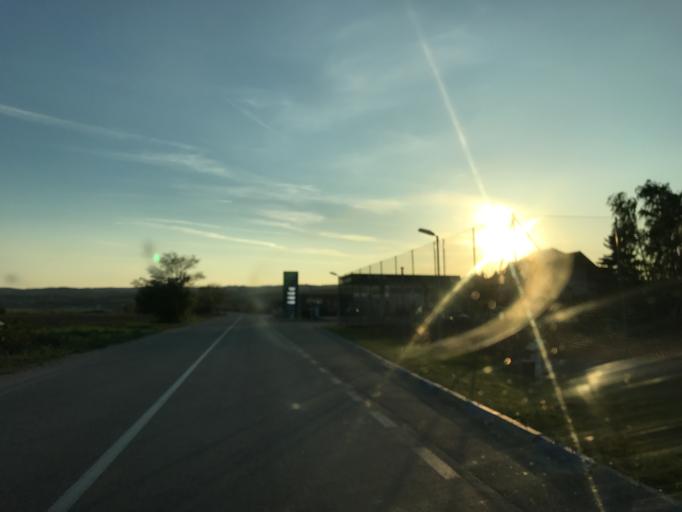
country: RO
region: Mehedinti
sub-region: Comuna Burila Mare
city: Burila Mare
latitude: 44.4908
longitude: 22.4803
